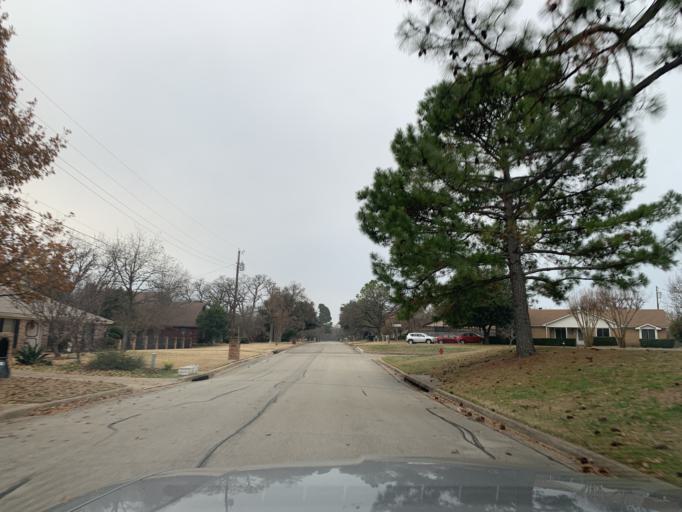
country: US
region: Texas
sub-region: Tarrant County
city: Bedford
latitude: 32.8355
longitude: -97.1523
